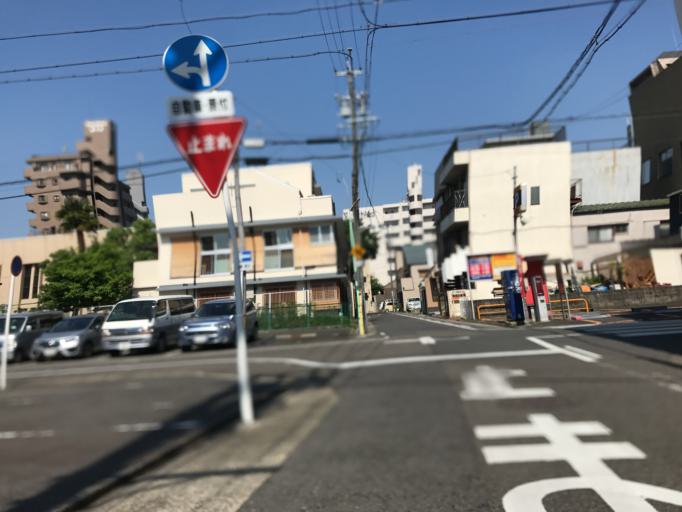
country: JP
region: Aichi
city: Nagoya-shi
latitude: 35.1772
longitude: 136.9236
